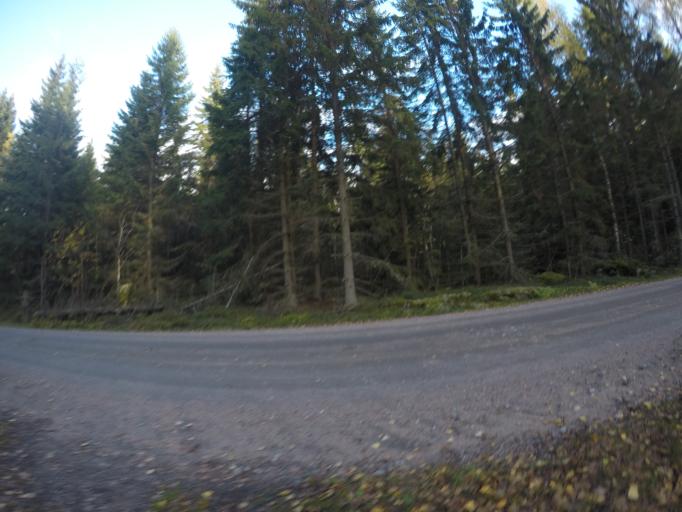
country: SE
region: Vaestmanland
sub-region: Arboga Kommun
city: Tyringe
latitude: 59.3459
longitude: 15.9604
